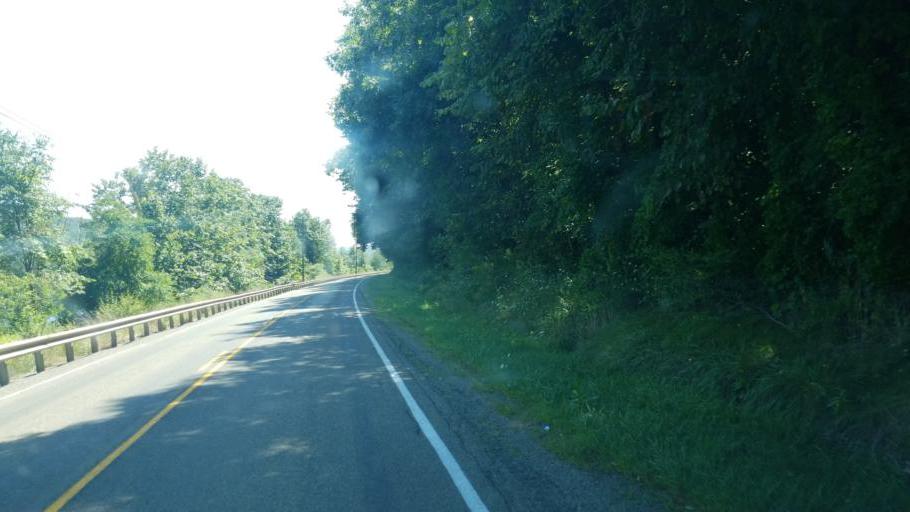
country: US
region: Pennsylvania
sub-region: Butler County
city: Chicora
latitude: 41.1160
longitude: -79.6797
